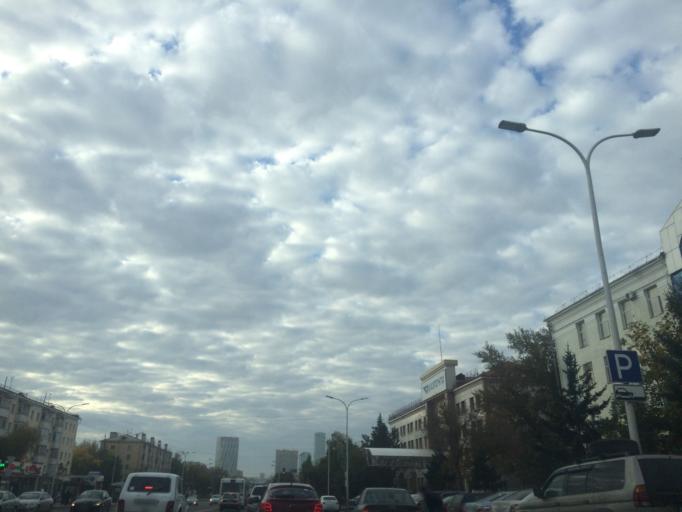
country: KZ
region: Astana Qalasy
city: Astana
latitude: 51.1781
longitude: 71.4179
